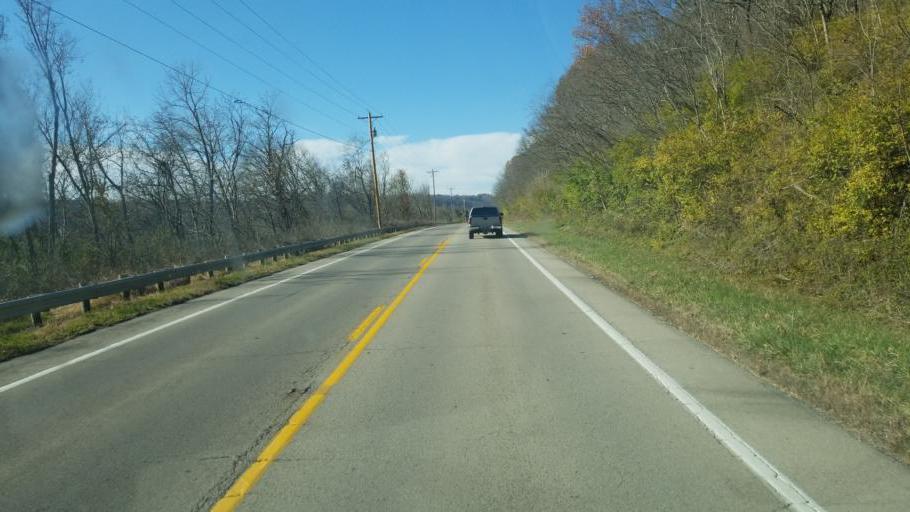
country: US
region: Kentucky
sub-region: Mason County
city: Maysville
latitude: 38.6504
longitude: -83.7458
